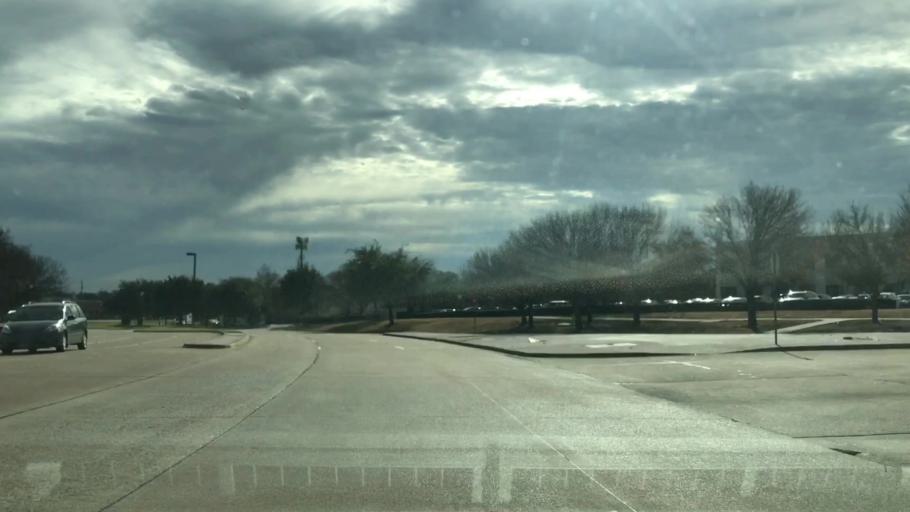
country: US
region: Texas
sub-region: Dallas County
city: Coppell
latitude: 32.9213
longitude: -96.9980
